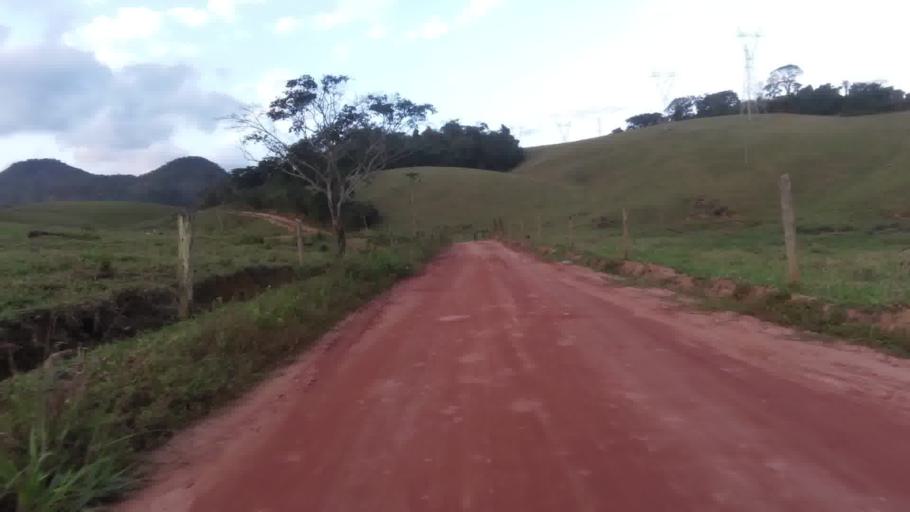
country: BR
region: Espirito Santo
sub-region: Guarapari
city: Guarapari
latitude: -20.6707
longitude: -40.6121
